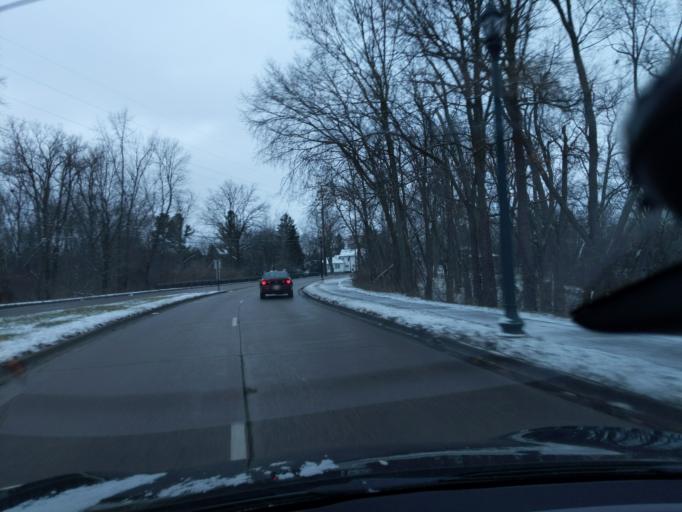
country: US
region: Michigan
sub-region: Ingham County
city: Okemos
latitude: 42.7136
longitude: -84.4309
